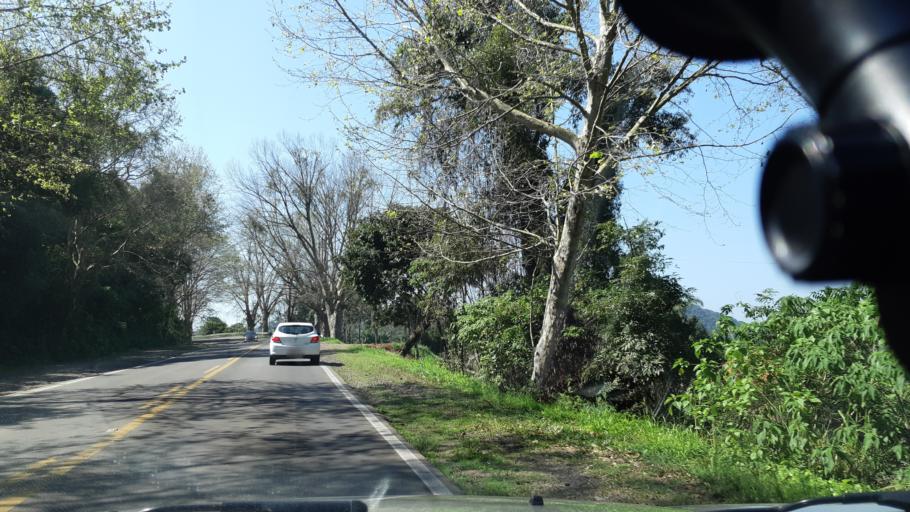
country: BR
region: Rio Grande do Sul
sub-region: Nova Petropolis
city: Nova Petropolis
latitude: -29.4051
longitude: -51.1267
